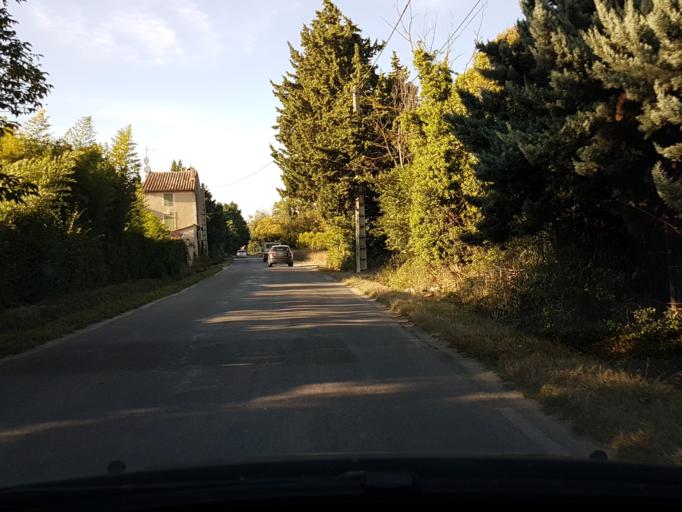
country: FR
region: Provence-Alpes-Cote d'Azur
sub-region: Departement des Bouches-du-Rhone
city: Molleges
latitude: 43.8130
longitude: 4.9486
